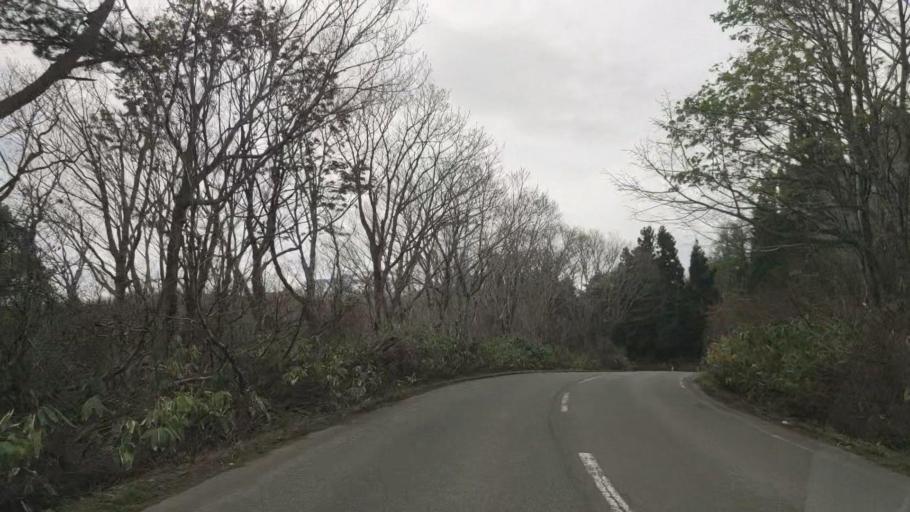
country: JP
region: Aomori
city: Aomori Shi
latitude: 40.7268
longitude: 140.8487
